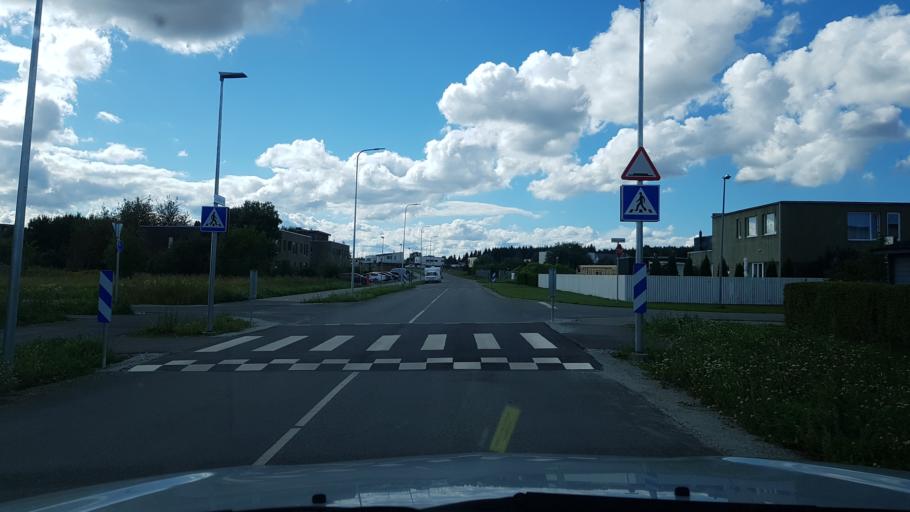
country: EE
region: Harju
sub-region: Tallinna linn
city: Tallinn
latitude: 59.3934
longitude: 24.8029
